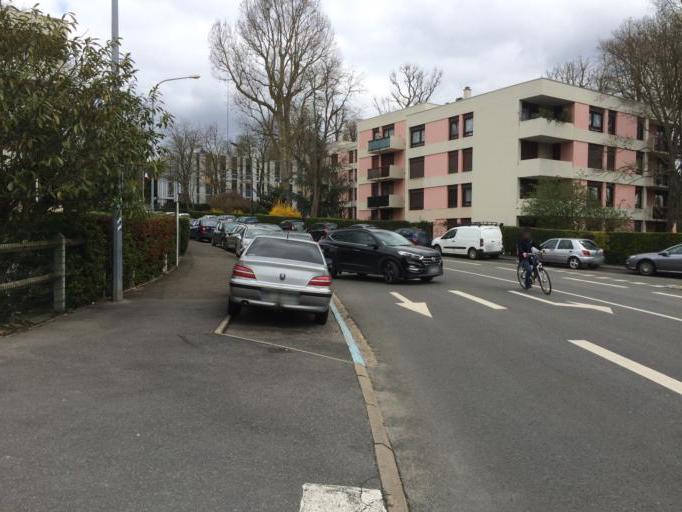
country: FR
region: Ile-de-France
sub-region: Departement de l'Essonne
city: Palaiseau
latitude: 48.7146
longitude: 2.2497
